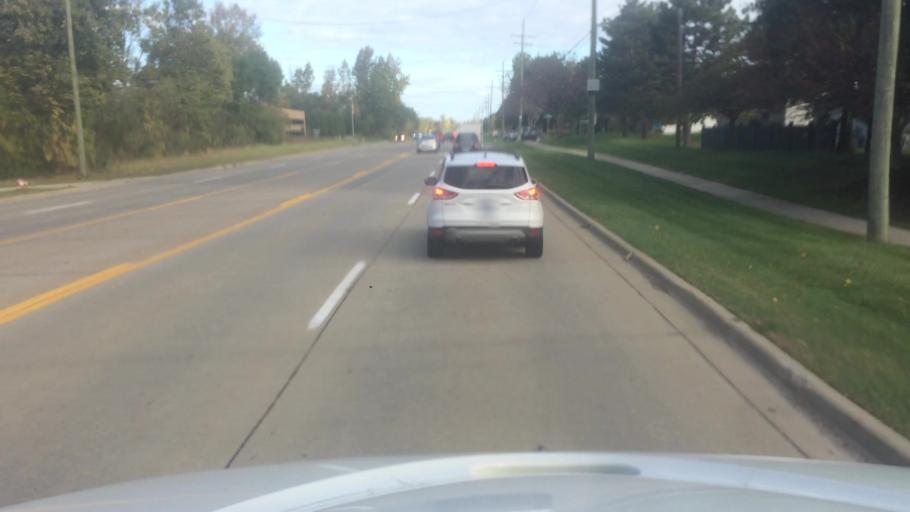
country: US
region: Michigan
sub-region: Macomb County
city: Shelby
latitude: 42.6626
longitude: -82.9943
